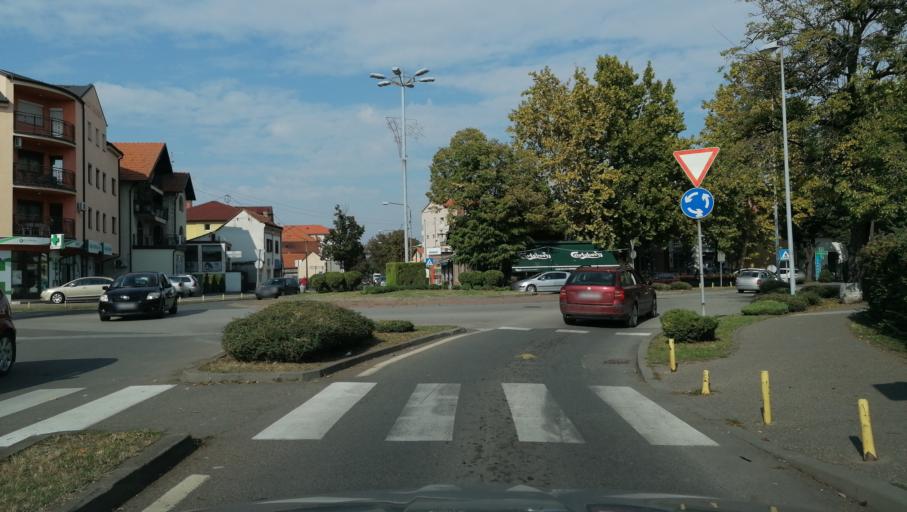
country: BA
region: Republika Srpska
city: Bijeljina
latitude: 44.7608
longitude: 19.2252
